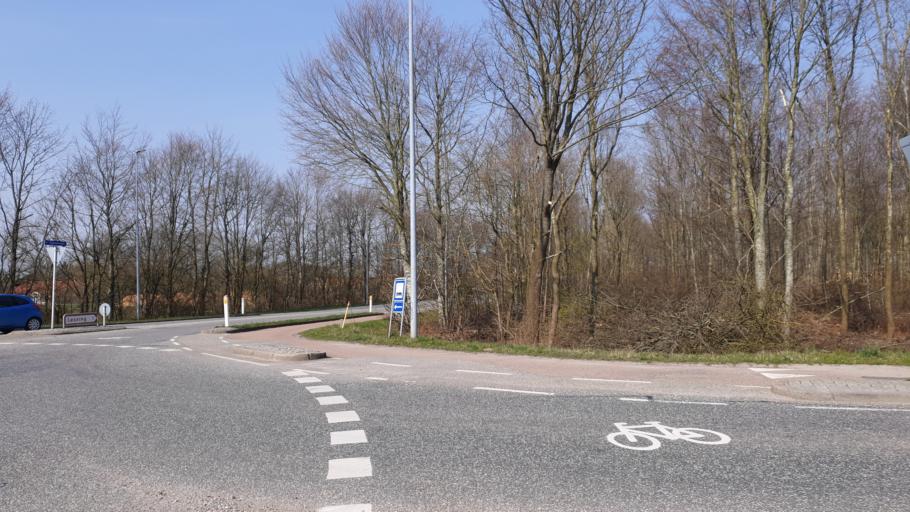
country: DK
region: Central Jutland
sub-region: Hedensted Kommune
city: Hedensted
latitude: 55.7811
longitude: 9.6970
